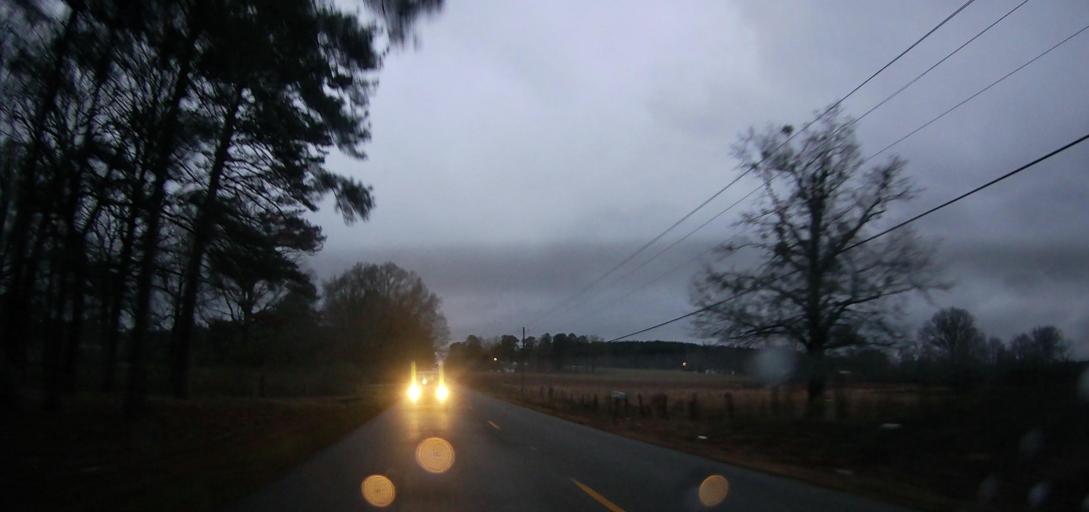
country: US
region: Alabama
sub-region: Tuscaloosa County
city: Vance
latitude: 33.1566
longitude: -87.2299
